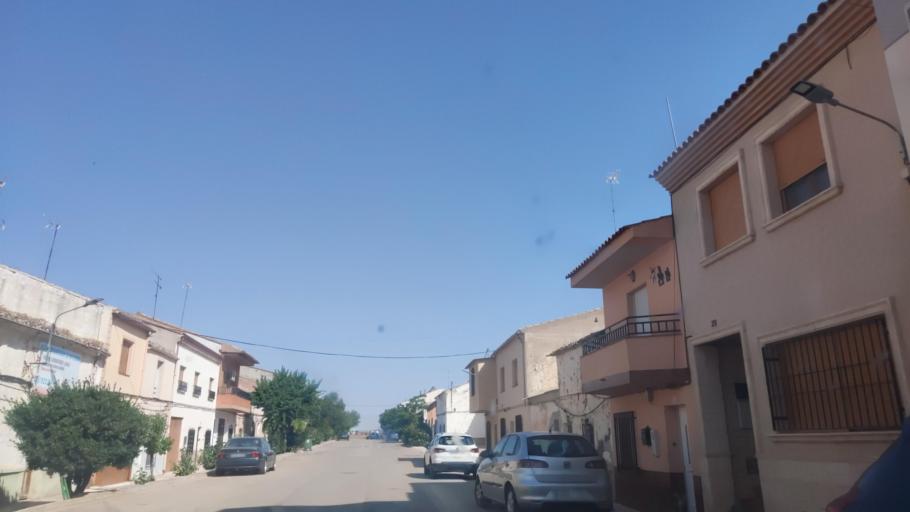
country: ES
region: Castille-La Mancha
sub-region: Provincia de Albacete
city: La Gineta
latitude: 39.1158
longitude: -1.9988
